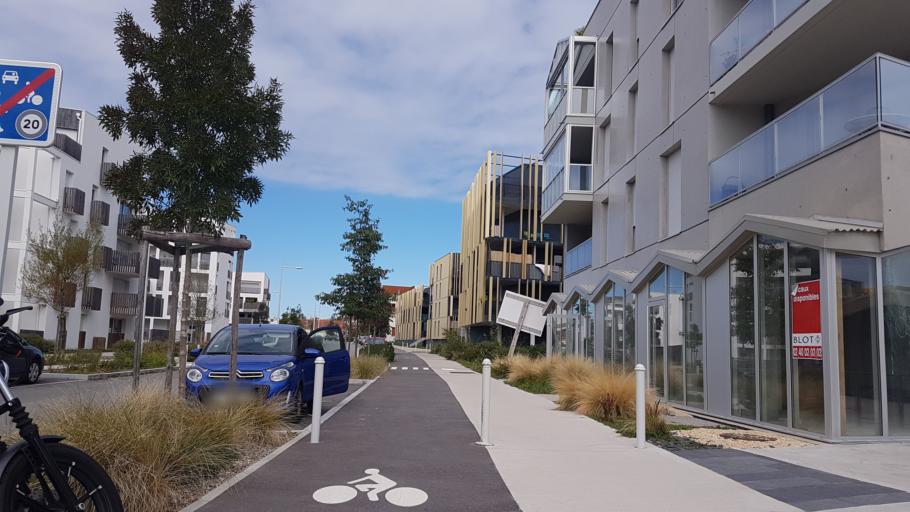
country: FR
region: Pays de la Loire
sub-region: Departement de la Loire-Atlantique
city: Reze
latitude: 47.1741
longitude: -1.5631
